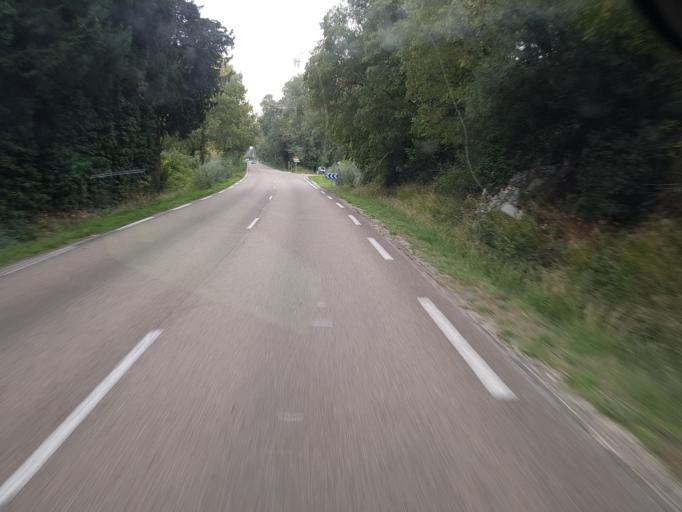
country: FR
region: Provence-Alpes-Cote d'Azur
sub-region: Departement des Bouches-du-Rhone
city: Barbentane
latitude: 43.9270
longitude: 4.7378
